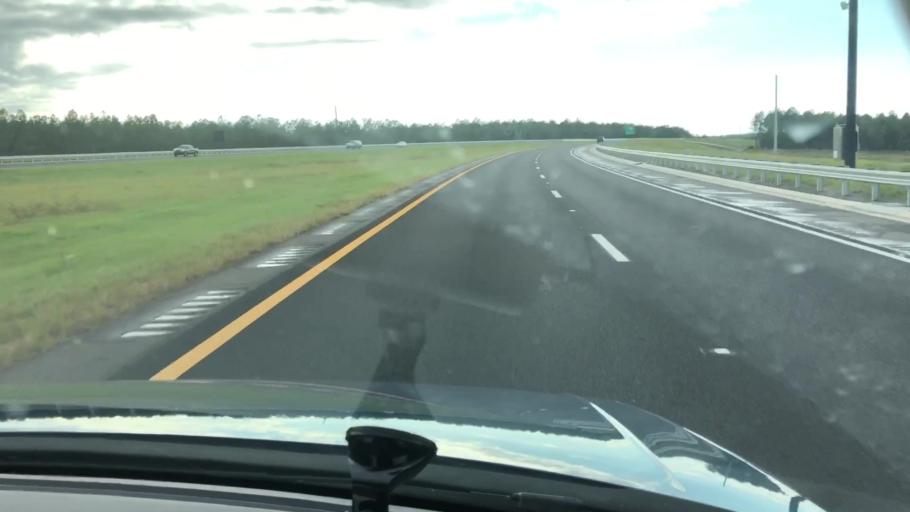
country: US
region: Florida
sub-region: Lake County
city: Mount Plymouth
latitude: 28.7773
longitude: -81.5279
